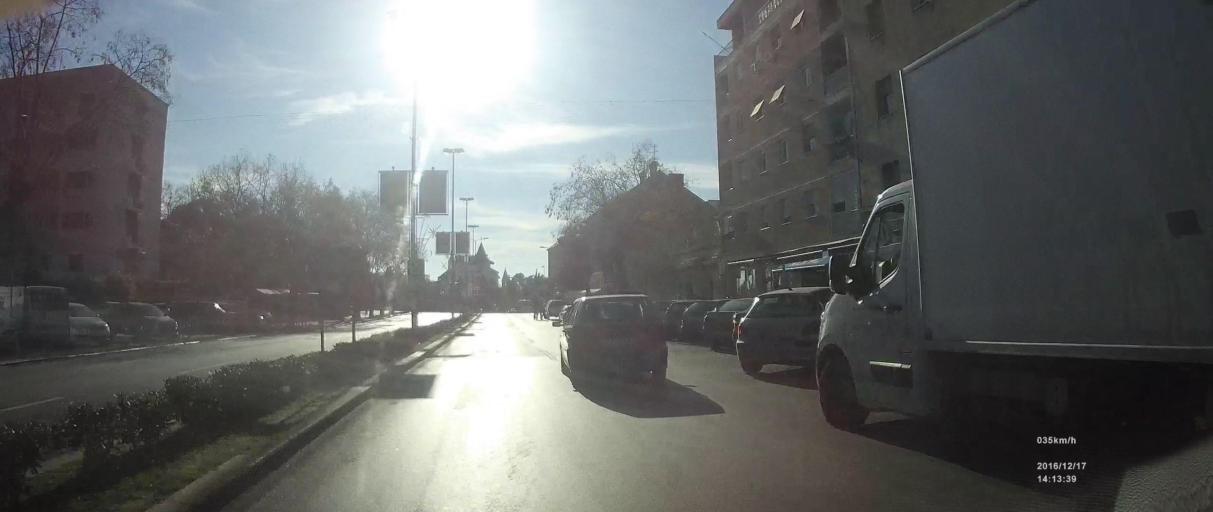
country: HR
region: Splitsko-Dalmatinska
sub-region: Grad Split
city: Split
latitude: 43.5135
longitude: 16.4430
